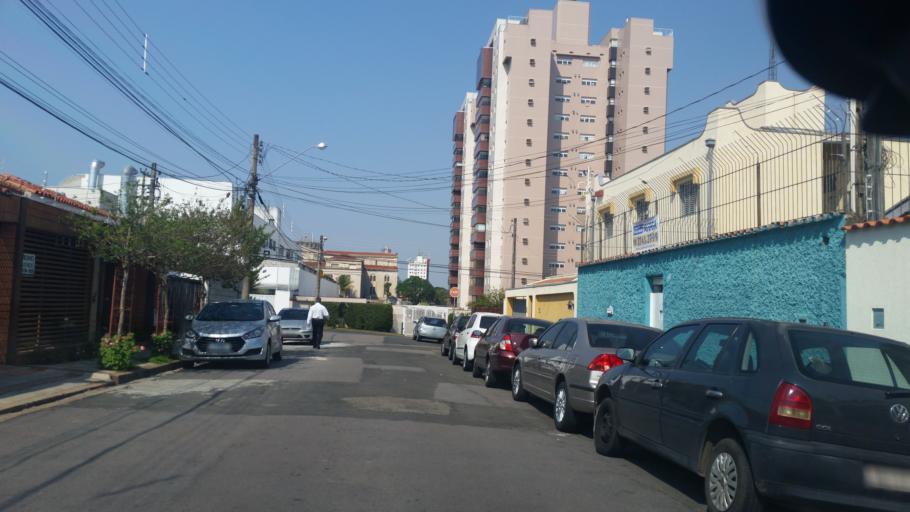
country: BR
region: Sao Paulo
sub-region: Campinas
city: Campinas
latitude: -22.8834
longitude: -47.0743
